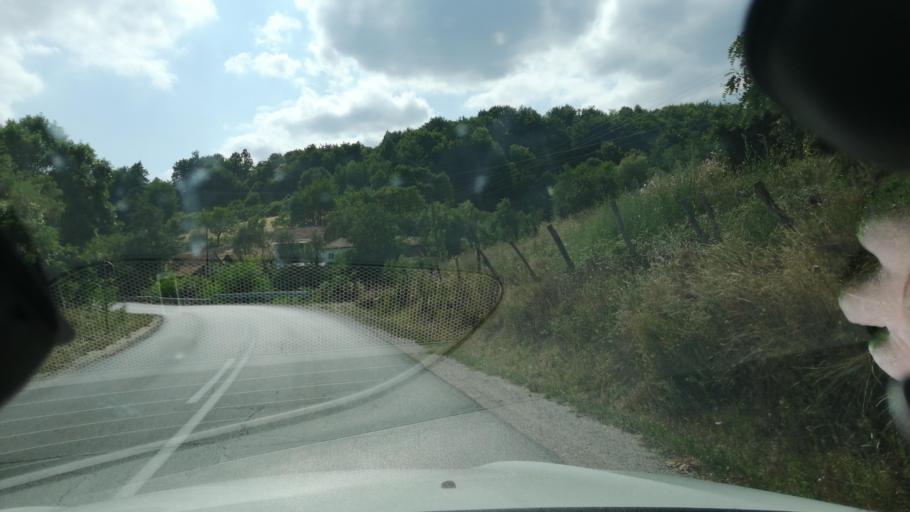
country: RS
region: Central Serbia
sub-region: Moravicki Okrug
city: Ivanjica
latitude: 43.6617
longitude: 20.2356
